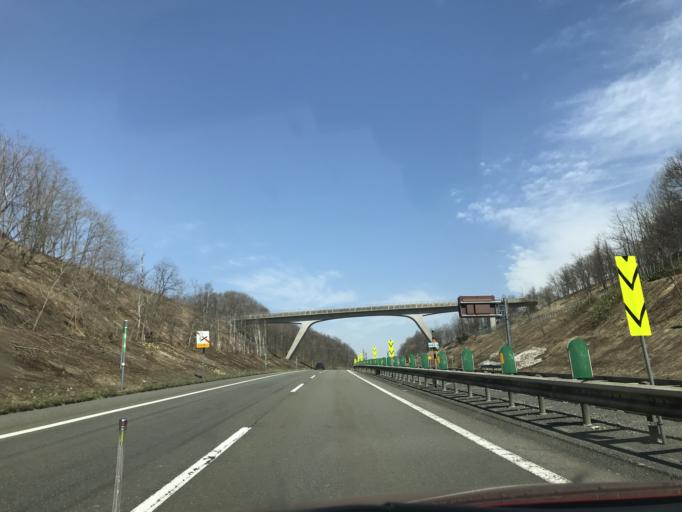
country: JP
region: Hokkaido
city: Bibai
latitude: 43.2491
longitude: 141.8308
